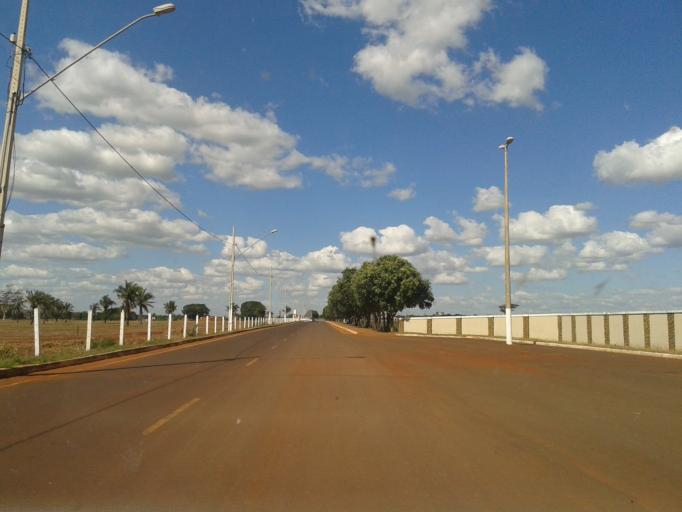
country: BR
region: Minas Gerais
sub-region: Santa Vitoria
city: Santa Vitoria
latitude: -18.6921
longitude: -49.9562
